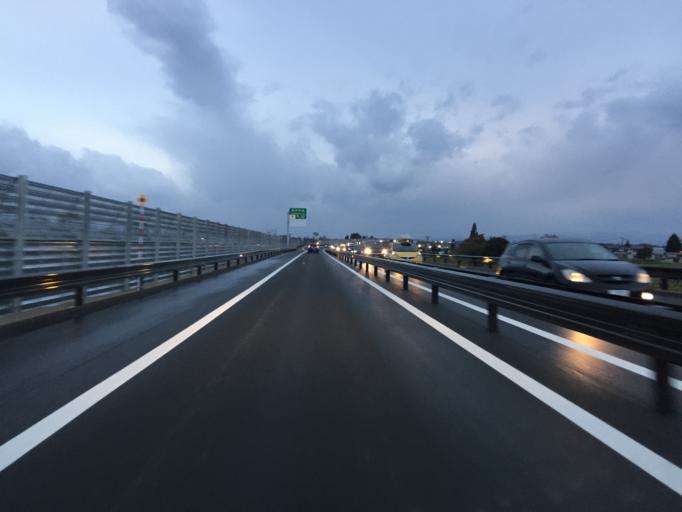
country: JP
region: Yamagata
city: Yonezawa
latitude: 37.9158
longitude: 140.1381
